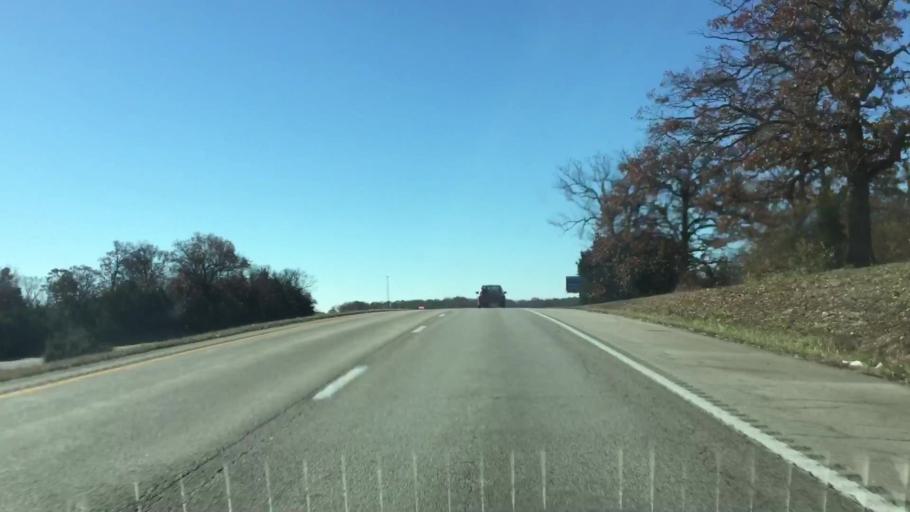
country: US
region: Missouri
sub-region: Cole County
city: Wardsville
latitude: 38.4552
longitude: -92.2994
